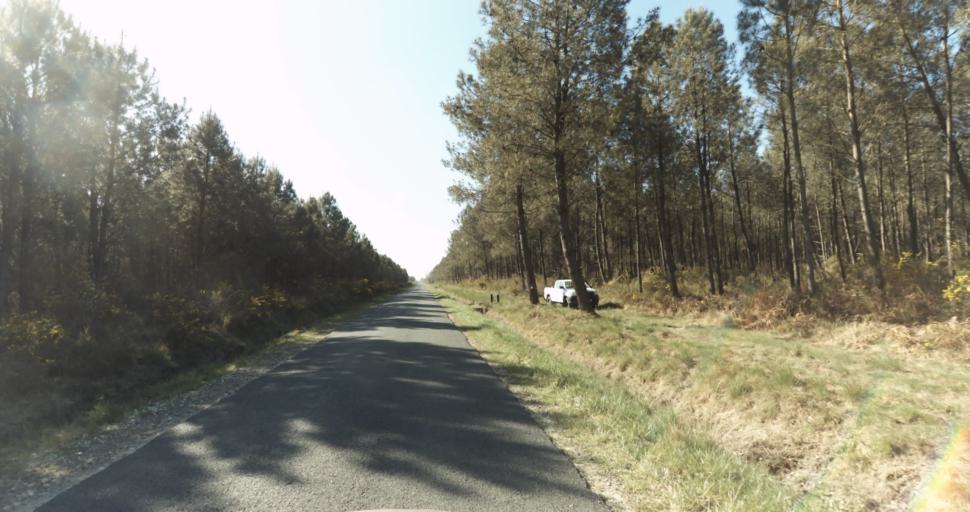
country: FR
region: Aquitaine
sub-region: Departement de la Gironde
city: Marcheprime
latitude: 44.7872
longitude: -0.8629
